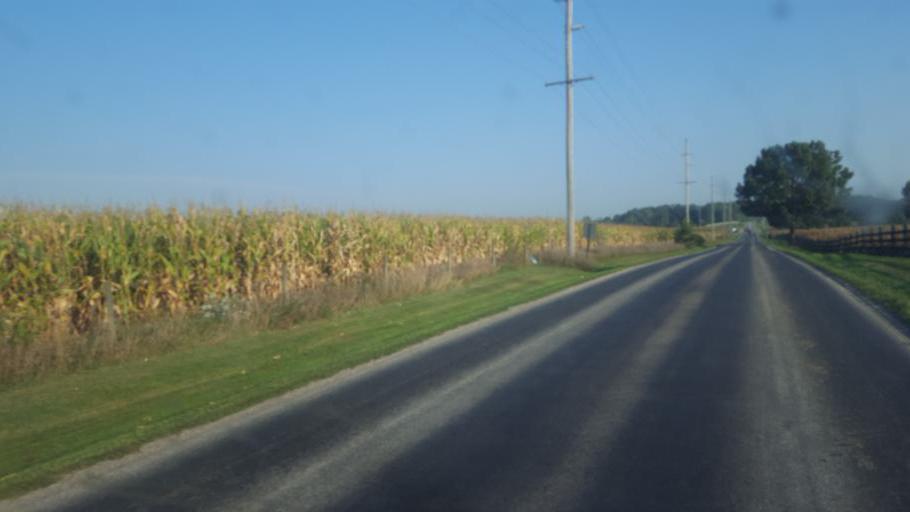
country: US
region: Indiana
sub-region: LaGrange County
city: Topeka
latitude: 41.6732
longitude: -85.5563
